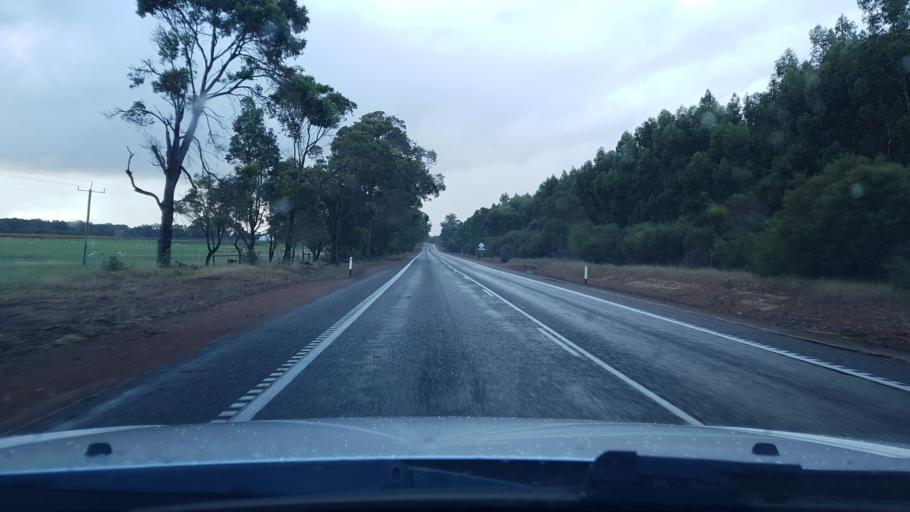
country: AU
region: Western Australia
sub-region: Augusta-Margaret River Shire
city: Margaret River
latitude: -33.8890
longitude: 115.0871
